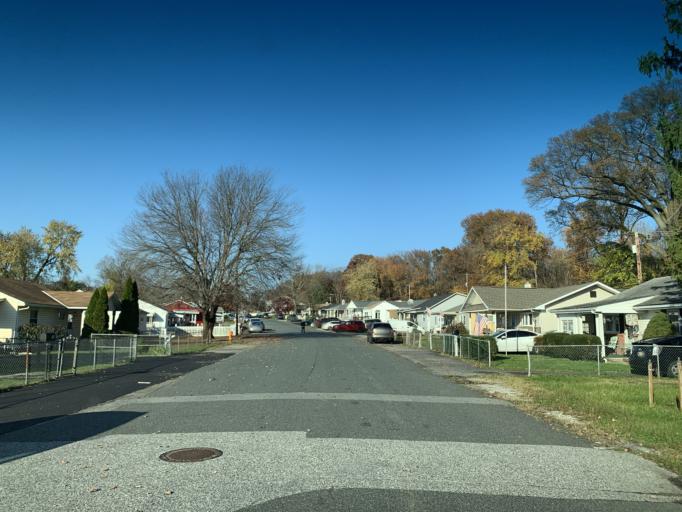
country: US
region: Maryland
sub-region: Baltimore County
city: Middle River
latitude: 39.3379
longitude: -76.4542
